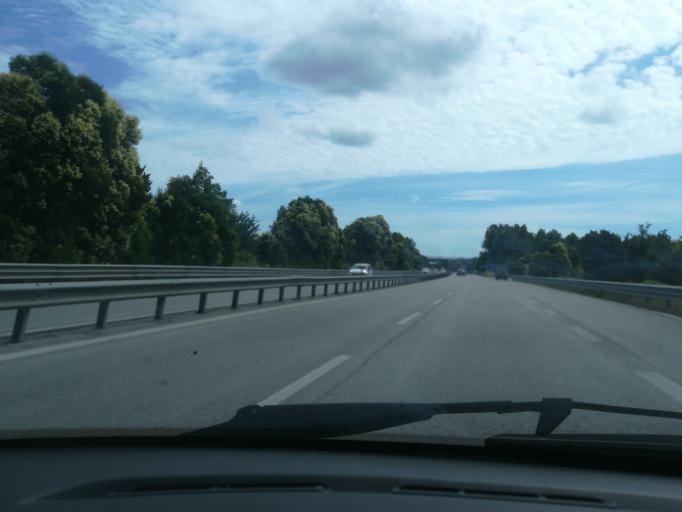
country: IT
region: The Marches
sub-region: Provincia di Macerata
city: Villa San Filippo
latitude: 43.2639
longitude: 13.5823
